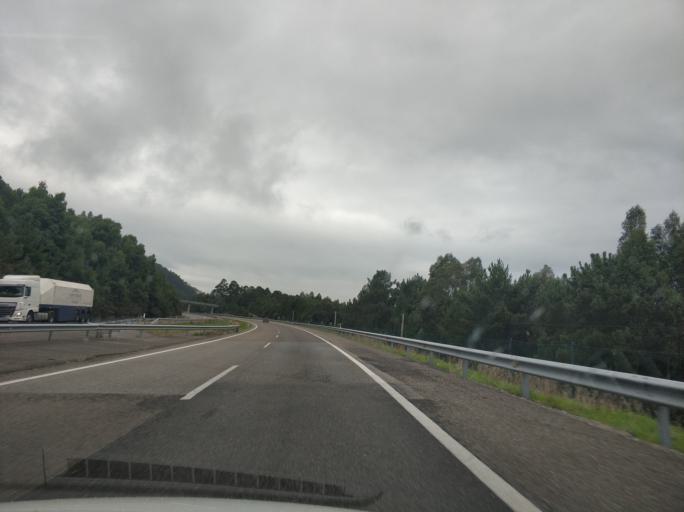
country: ES
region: Galicia
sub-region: Provincia de Lugo
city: Ribadeo
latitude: 43.5350
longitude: -7.1130
